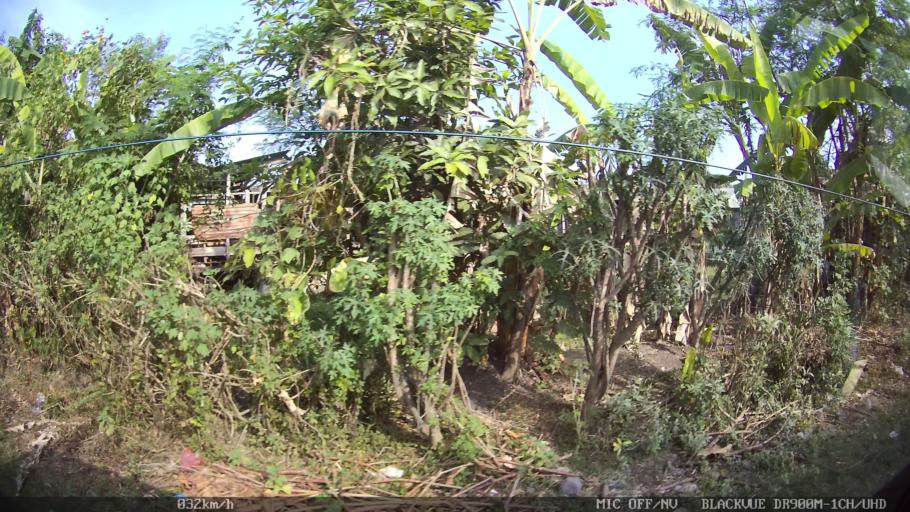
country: ID
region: Daerah Istimewa Yogyakarta
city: Kasihan
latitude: -7.8374
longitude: 110.3194
